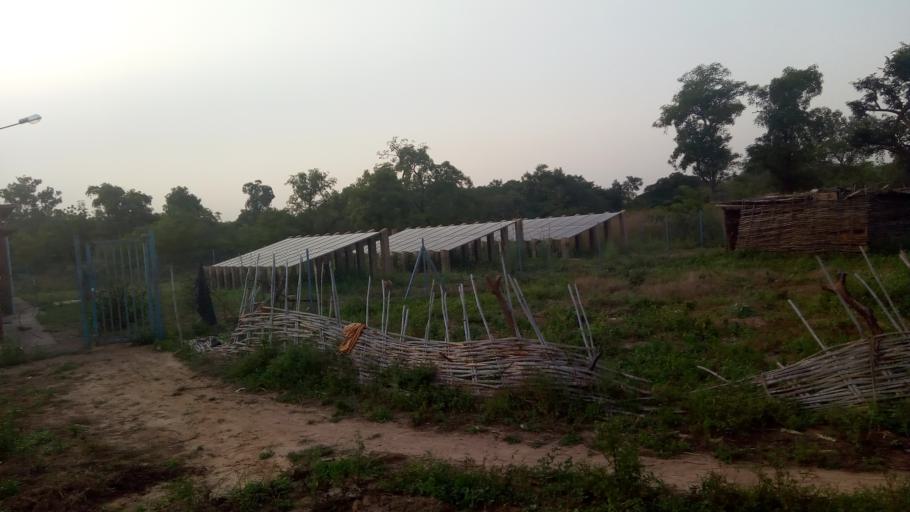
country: ML
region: Kayes
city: Kita
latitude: 13.1394
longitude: -8.8427
